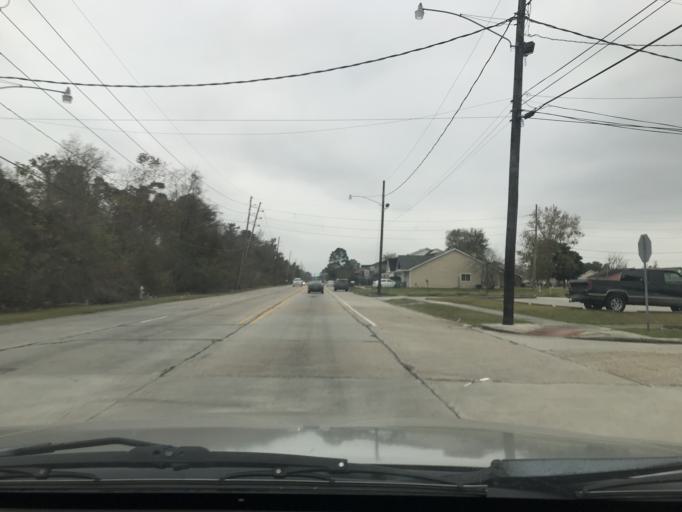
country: US
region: Louisiana
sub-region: Jefferson Parish
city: Woodmere
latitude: 29.8619
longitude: -90.0729
